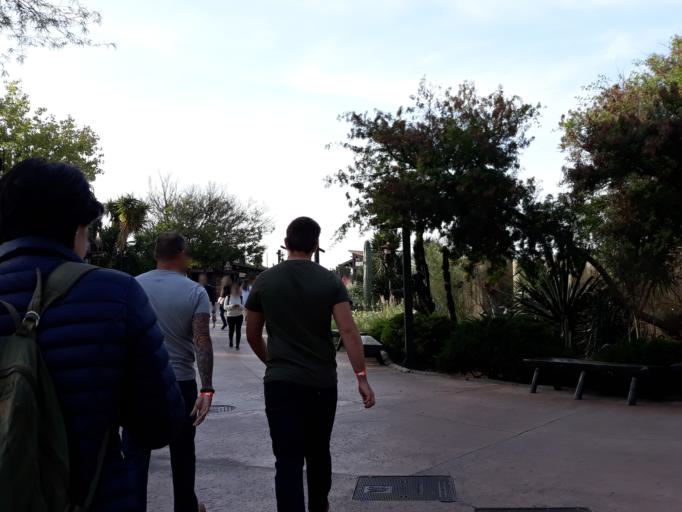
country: ES
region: Catalonia
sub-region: Provincia de Tarragona
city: Salou
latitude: 41.0871
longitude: 1.1568
